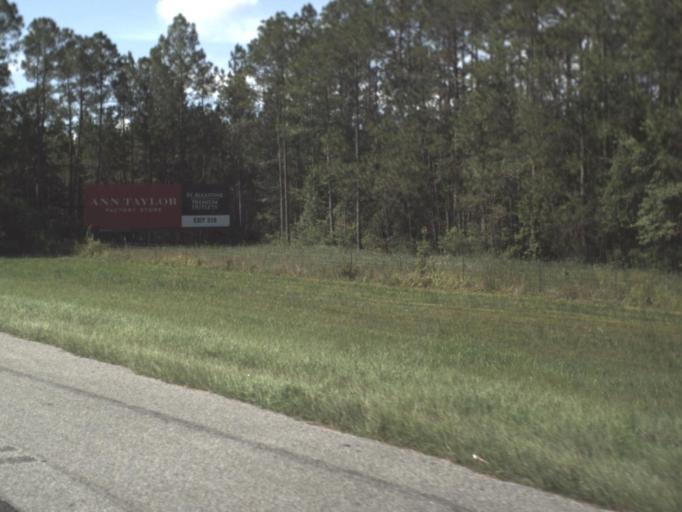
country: US
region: Florida
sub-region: Saint Johns County
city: Fruit Cove
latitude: 30.0337
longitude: -81.4907
